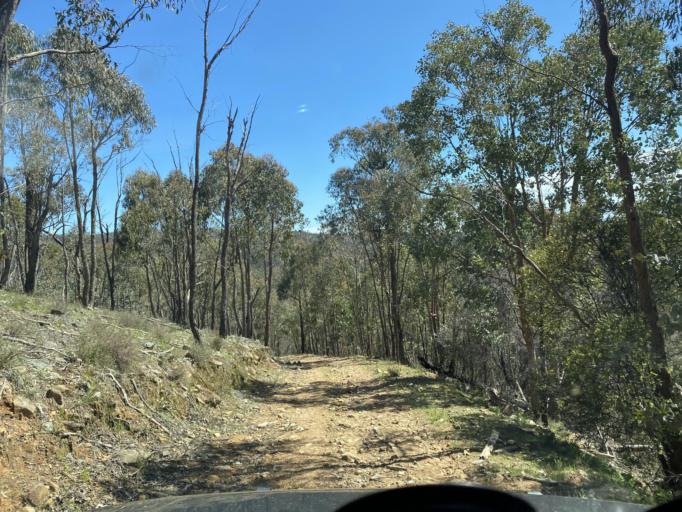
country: AU
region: Victoria
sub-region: Benalla
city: Benalla
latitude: -36.7195
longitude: 146.1818
